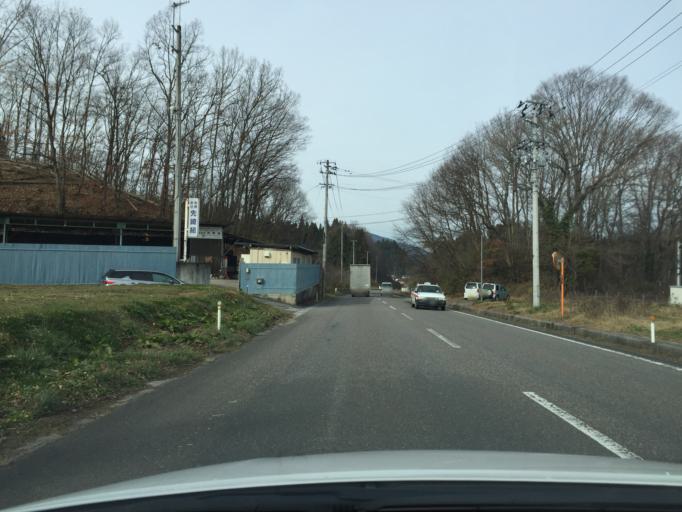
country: JP
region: Fukushima
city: Funehikimachi-funehiki
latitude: 37.2757
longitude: 140.6267
